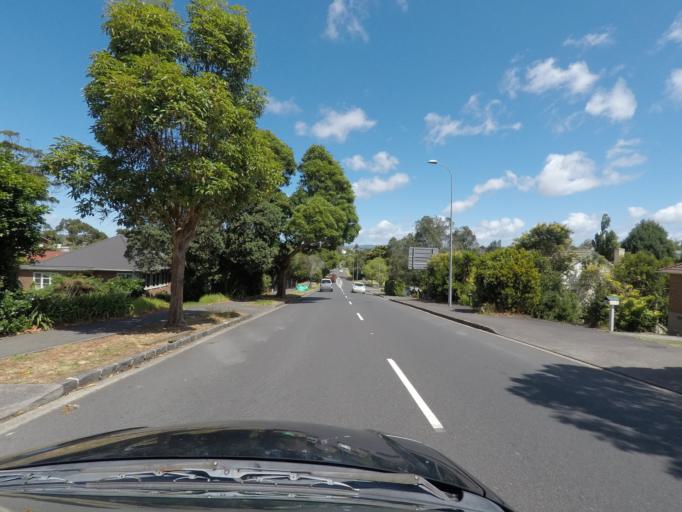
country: NZ
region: Auckland
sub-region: Auckland
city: Auckland
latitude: -36.8562
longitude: 174.7193
